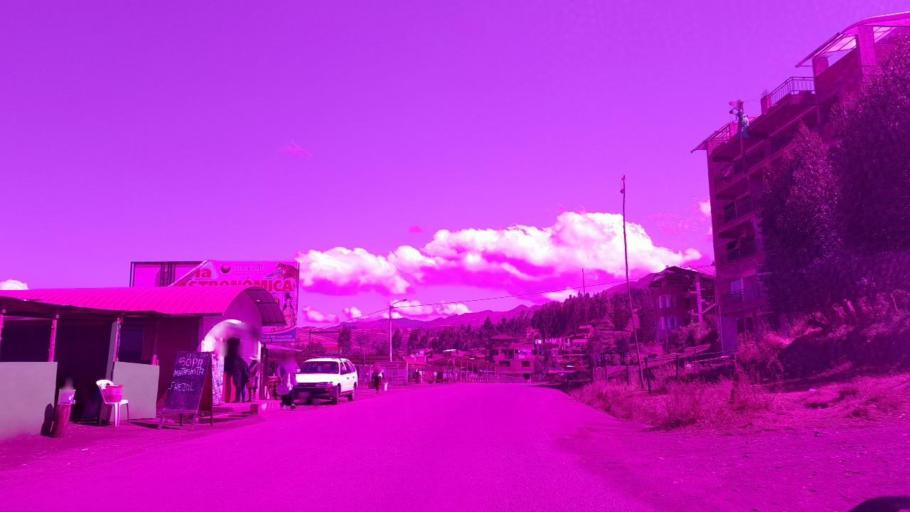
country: PE
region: Cusco
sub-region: Provincia de Cusco
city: Cusco
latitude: -13.5043
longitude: -71.9217
